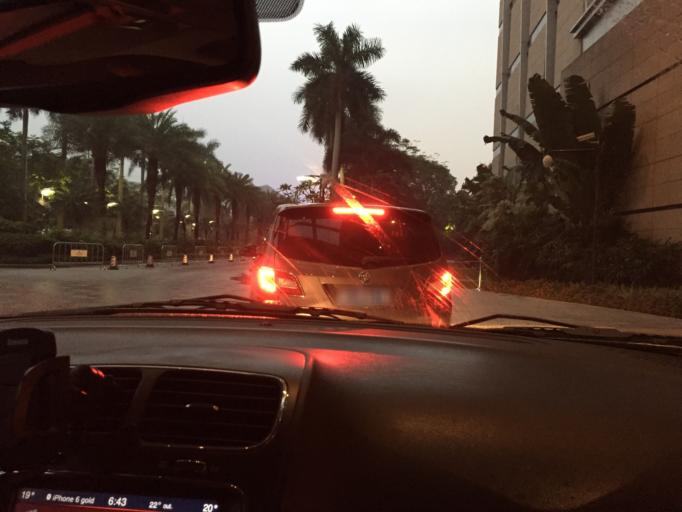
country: CN
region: Guangdong
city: Huangcun
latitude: 23.1048
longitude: 113.3644
